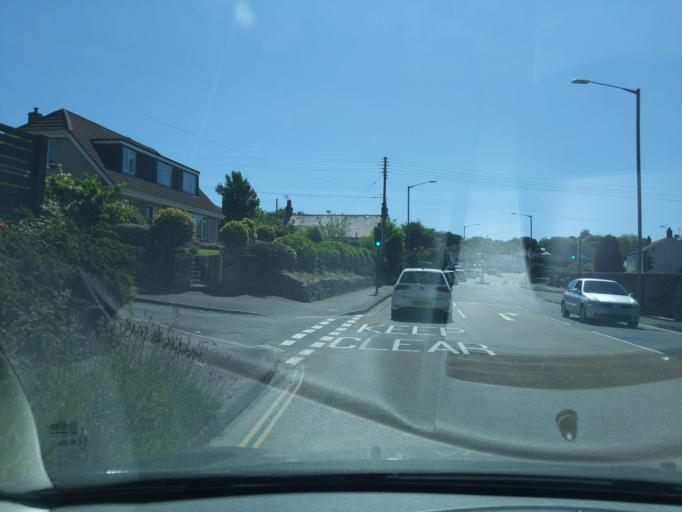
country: GB
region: England
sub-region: Cornwall
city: St Austell
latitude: 50.3407
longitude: -4.7552
